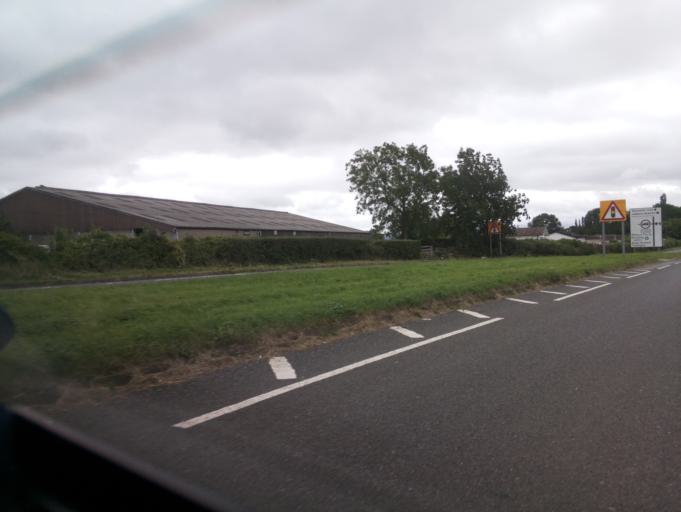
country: GB
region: England
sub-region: Gloucestershire
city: Tewkesbury
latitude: 51.9689
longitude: -2.1571
